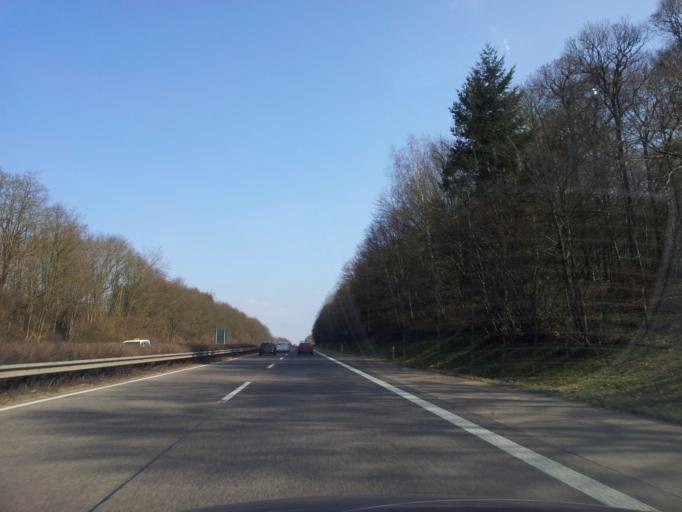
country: DE
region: Rheinland-Pfalz
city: Fohren
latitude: 49.8413
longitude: 6.7764
